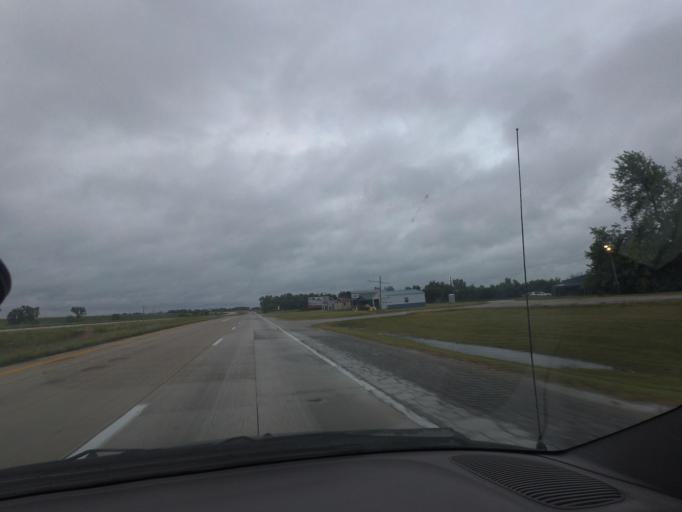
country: US
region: Missouri
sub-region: Marion County
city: Monroe City
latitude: 39.6686
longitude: -91.8530
